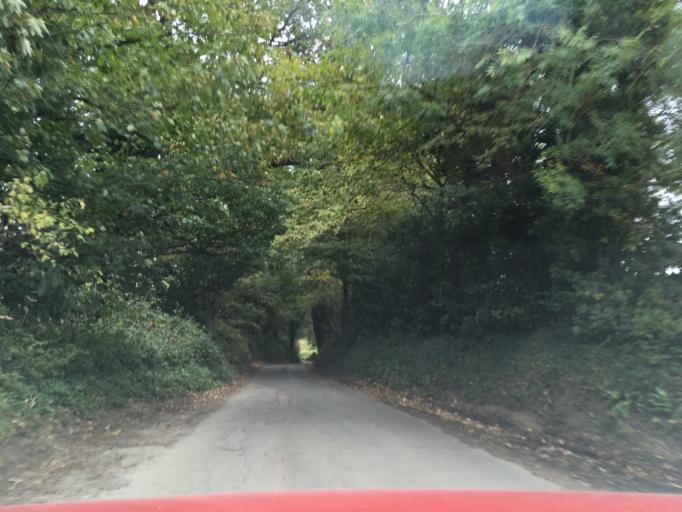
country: GB
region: England
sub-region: South Gloucestershire
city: Horton
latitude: 51.5883
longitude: -2.3387
